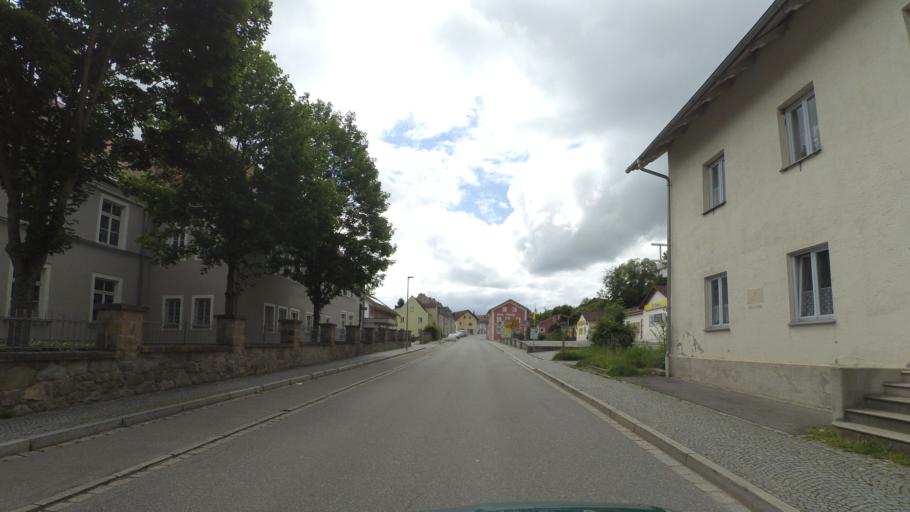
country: DE
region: Bavaria
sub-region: Lower Bavaria
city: Viechtach
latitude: 49.0750
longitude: 12.8898
